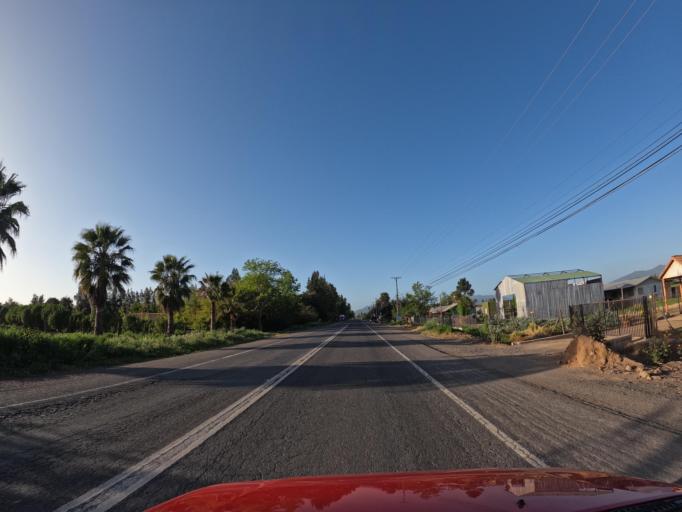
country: CL
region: O'Higgins
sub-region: Provincia de Colchagua
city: Santa Cruz
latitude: -34.4993
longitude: -71.3622
